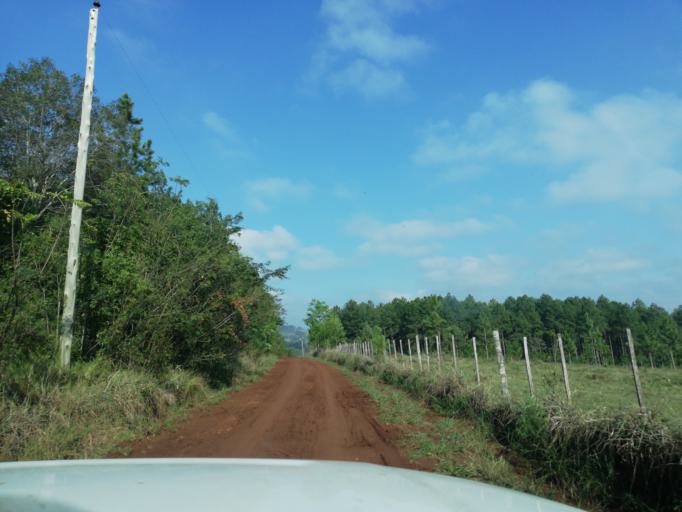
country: AR
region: Misiones
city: Cerro Azul
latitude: -27.5926
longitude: -55.5161
